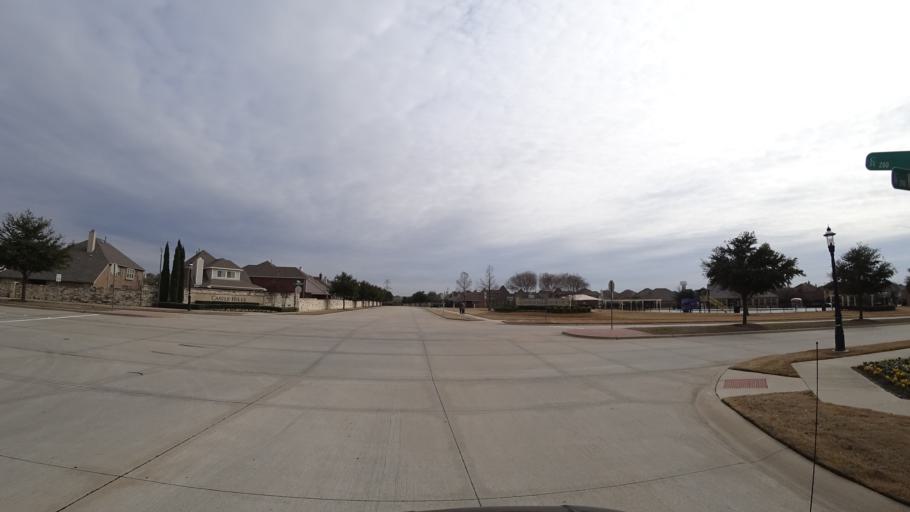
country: US
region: Texas
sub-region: Denton County
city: The Colony
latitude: 33.0555
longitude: -96.9051
